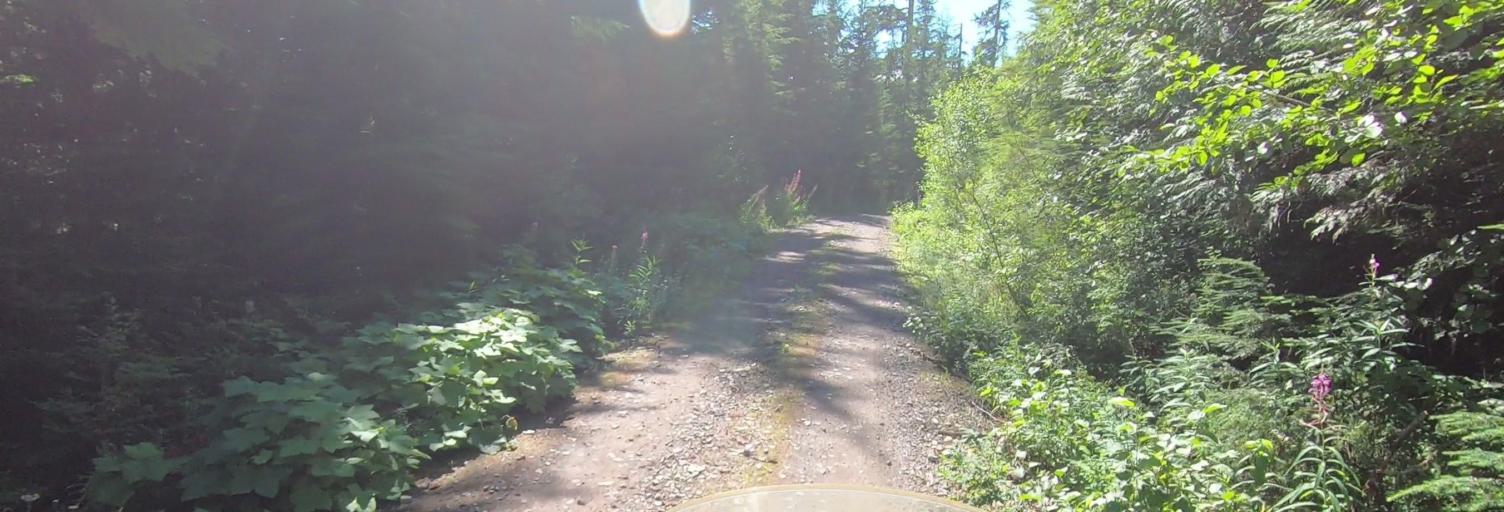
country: CA
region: British Columbia
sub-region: Fraser Valley Regional District
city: Chilliwack
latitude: 48.8566
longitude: -121.7932
